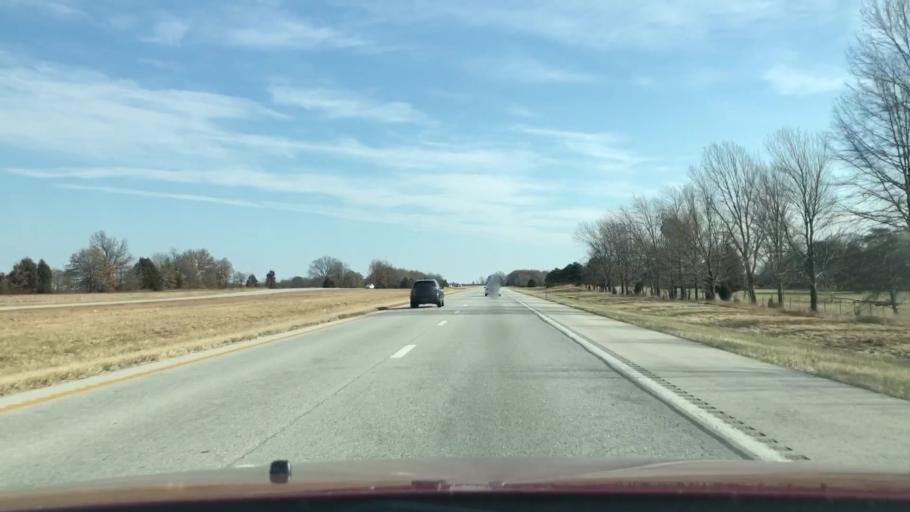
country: US
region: Missouri
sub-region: Webster County
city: Rogersville
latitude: 37.1232
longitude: -92.9924
